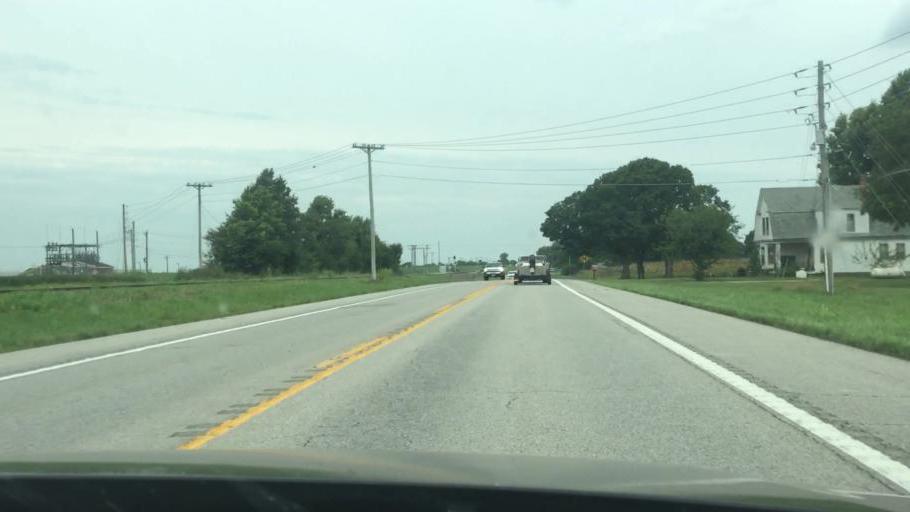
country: US
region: Missouri
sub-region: Pettis County
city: Sedalia
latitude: 38.6949
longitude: -93.1488
